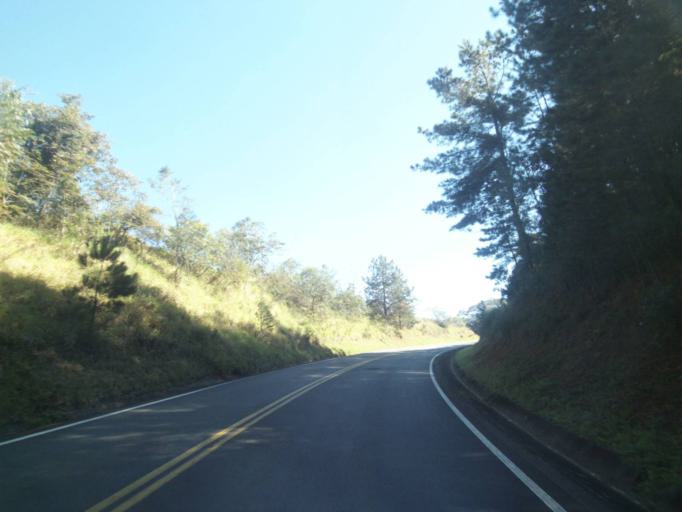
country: BR
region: Parana
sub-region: Tibagi
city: Tibagi
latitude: -24.4696
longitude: -50.5374
